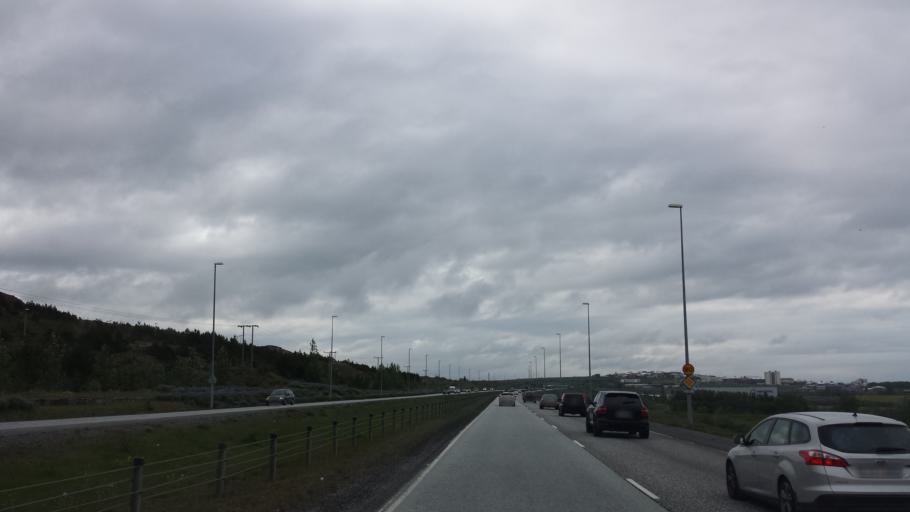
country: IS
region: Capital Region
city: Mosfellsbaer
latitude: 64.1524
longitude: -21.7390
